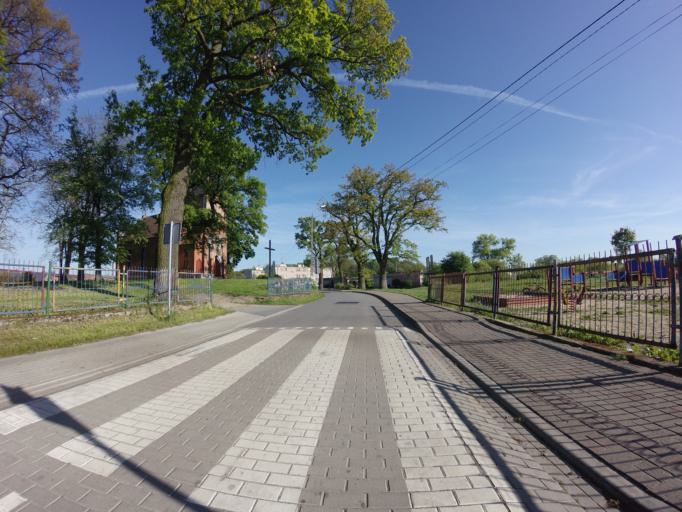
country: PL
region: West Pomeranian Voivodeship
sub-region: Powiat choszczenski
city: Pelczyce
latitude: 53.1183
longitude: 15.3224
